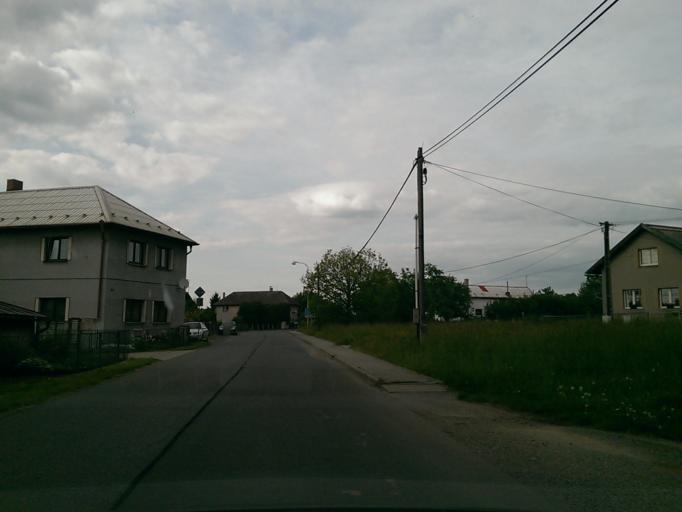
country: CZ
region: Central Bohemia
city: Bakov nad Jizerou
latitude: 50.4784
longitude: 14.8913
